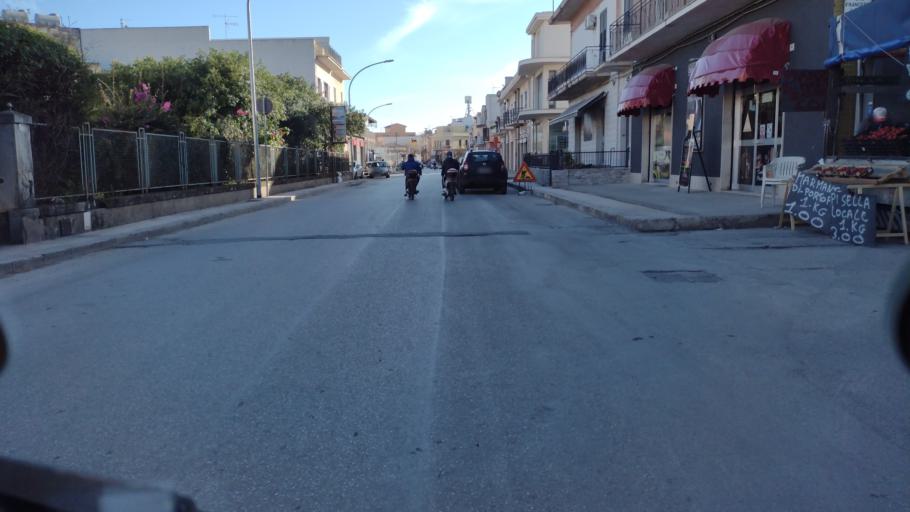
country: IT
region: Sicily
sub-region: Provincia di Siracusa
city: Avola
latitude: 36.9119
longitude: 15.1405
